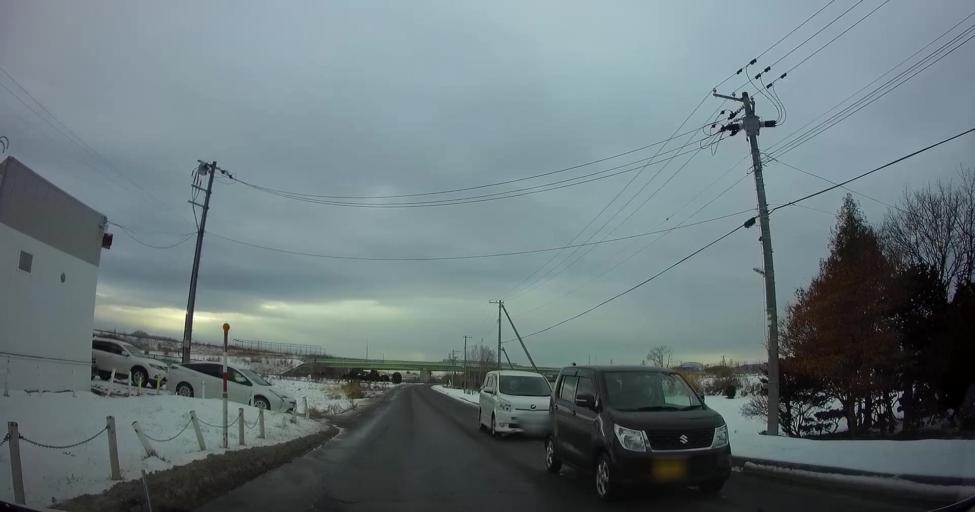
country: JP
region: Hokkaido
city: Nanae
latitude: 41.8365
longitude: 140.6917
